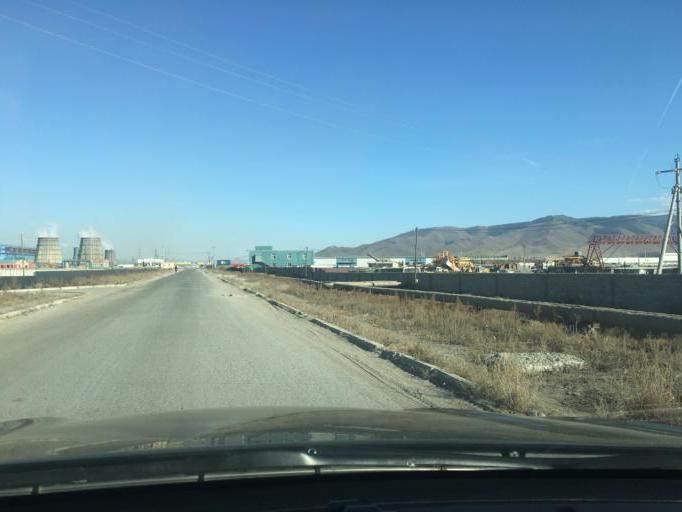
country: MN
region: Ulaanbaatar
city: Ulaanbaatar
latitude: 47.8880
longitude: 106.7812
